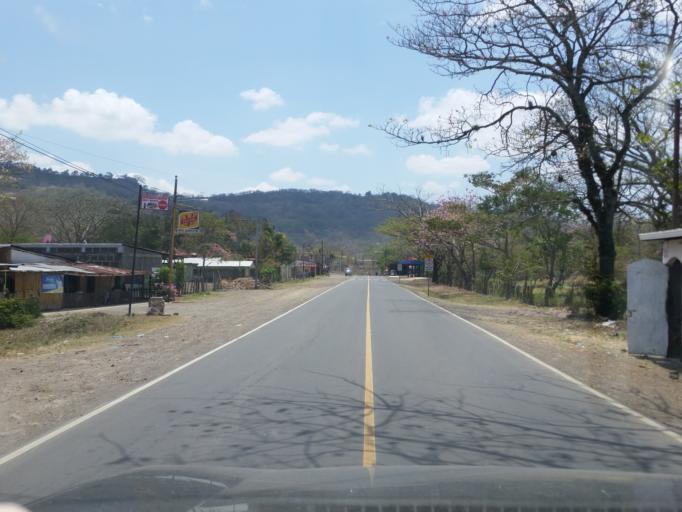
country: NI
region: Boaco
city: Boaco
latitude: 12.4781
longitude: -85.6451
